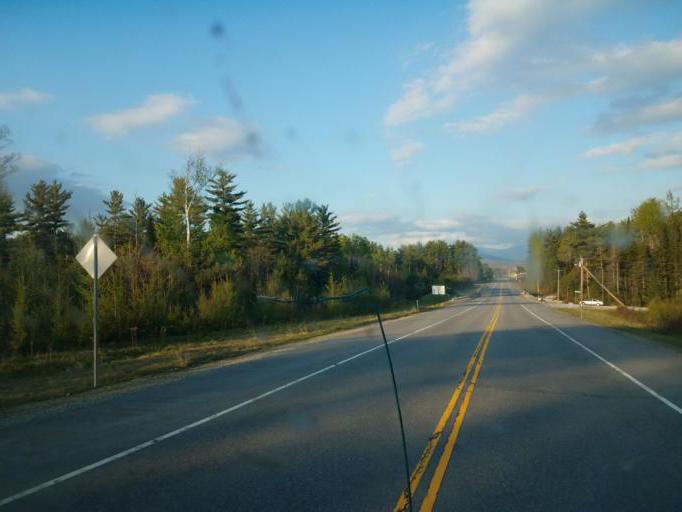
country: US
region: New Hampshire
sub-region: Grafton County
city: Deerfield
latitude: 44.2658
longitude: -71.5714
